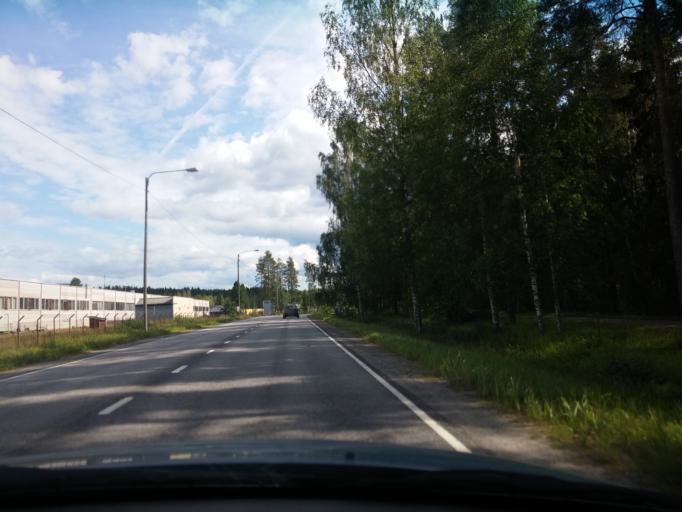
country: FI
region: Central Finland
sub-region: Keuruu
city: Keuruu
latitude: 62.2502
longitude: 24.7232
